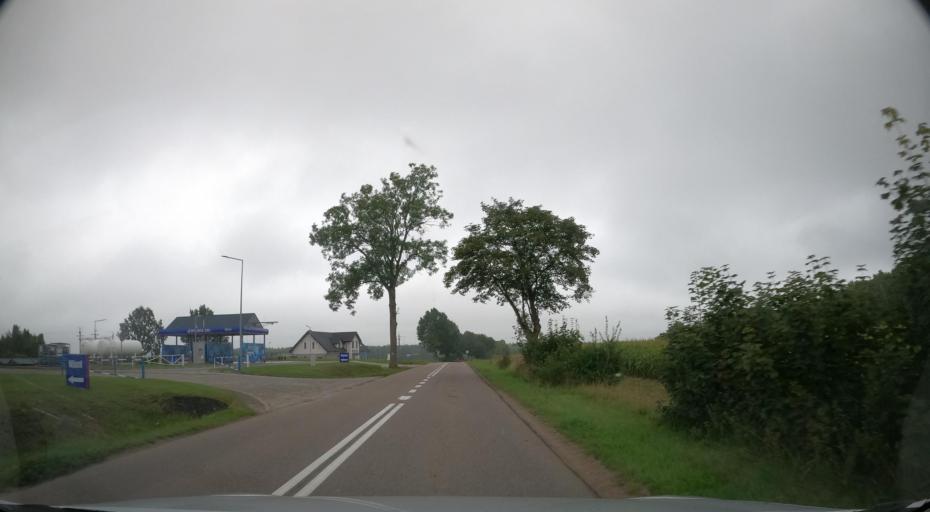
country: PL
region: Pomeranian Voivodeship
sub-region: Powiat wejherowski
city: Linia
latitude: 54.4574
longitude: 18.0376
